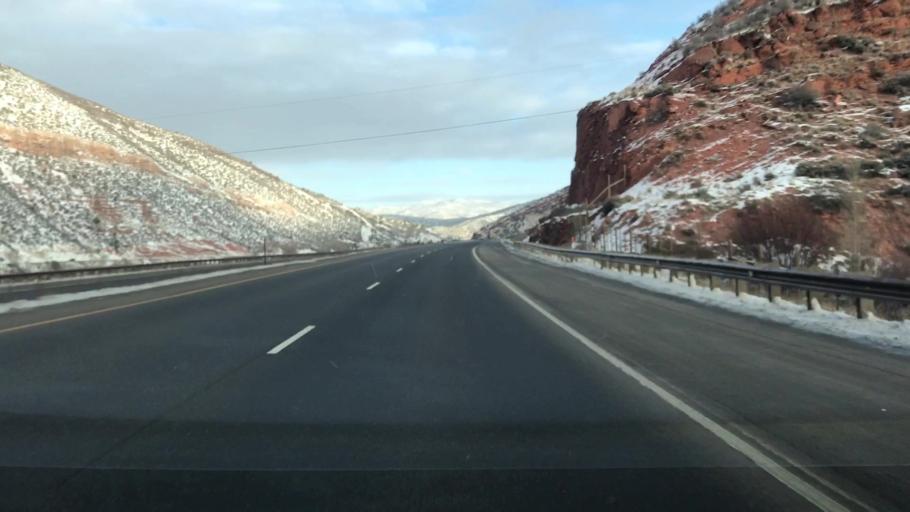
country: US
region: Colorado
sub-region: Eagle County
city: Edwards
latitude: 39.6665
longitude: -106.6437
